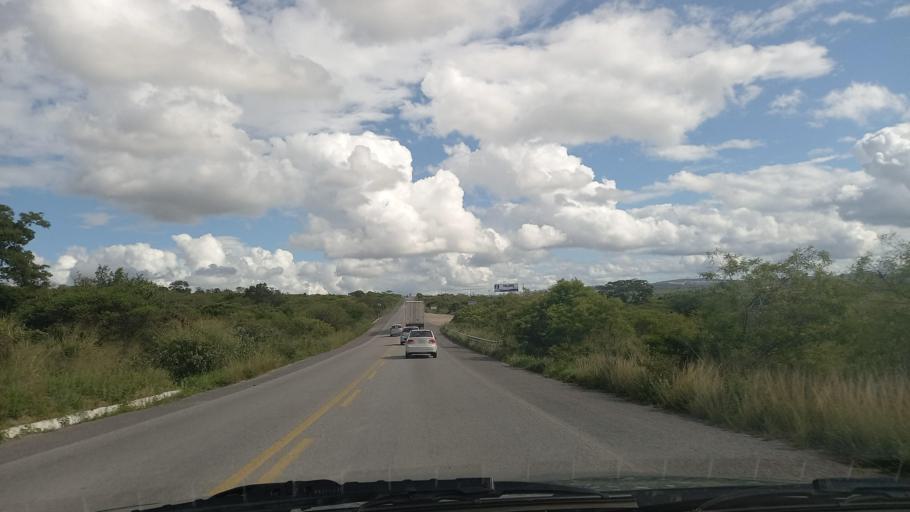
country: BR
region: Pernambuco
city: Garanhuns
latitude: -8.8119
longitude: -36.4449
